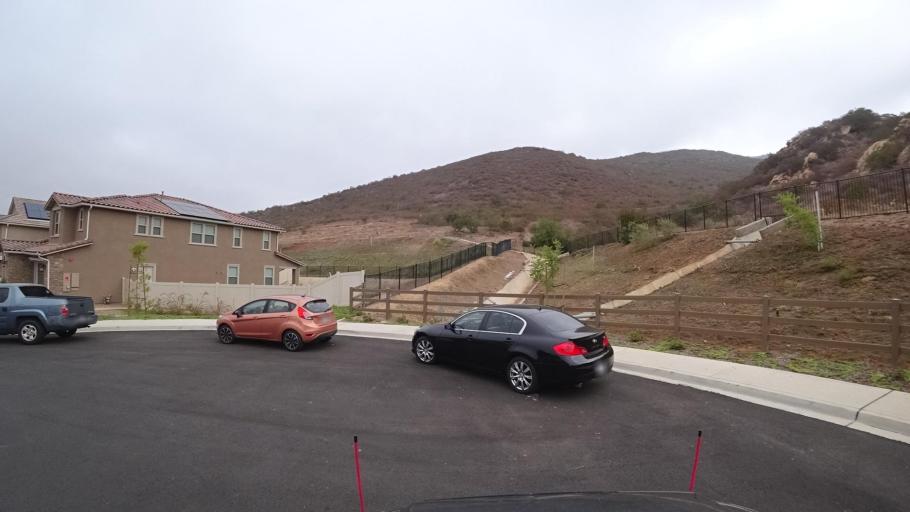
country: US
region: California
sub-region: San Diego County
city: Rainbow
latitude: 33.3633
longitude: -117.1540
